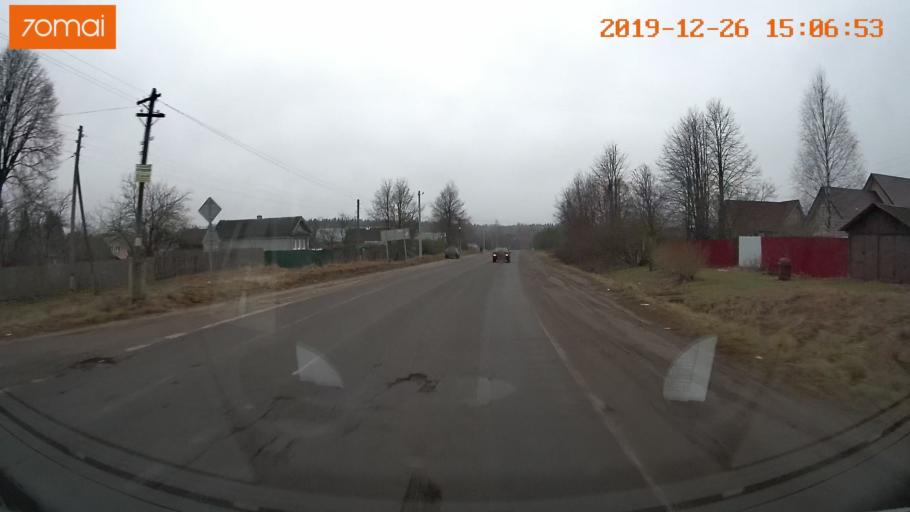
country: RU
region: Jaroslavl
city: Rybinsk
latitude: 58.1742
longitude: 38.8430
